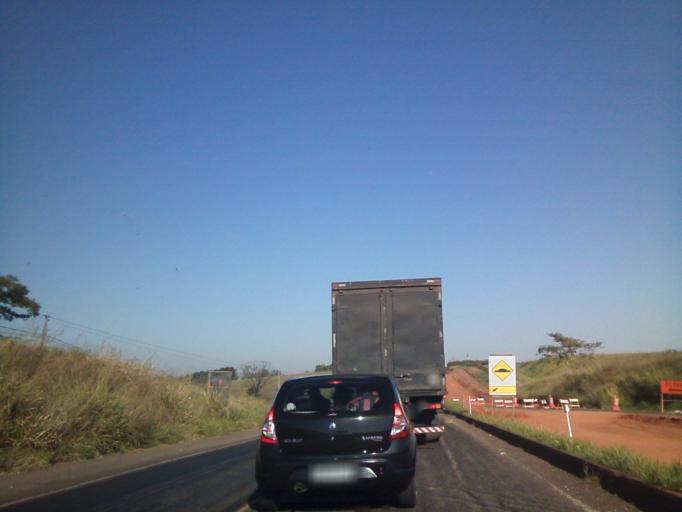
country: BR
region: Sao Paulo
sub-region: Presidente Prudente
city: Presidente Prudente
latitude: -22.1761
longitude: -51.4107
